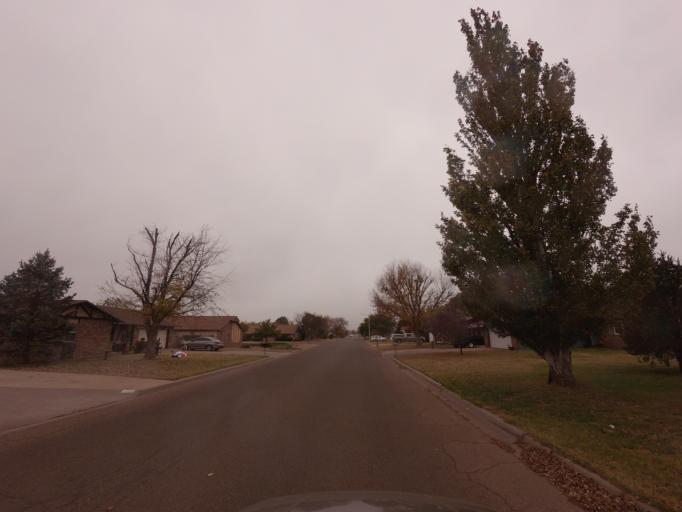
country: US
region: New Mexico
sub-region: Curry County
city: Clovis
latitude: 34.4262
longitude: -103.1843
